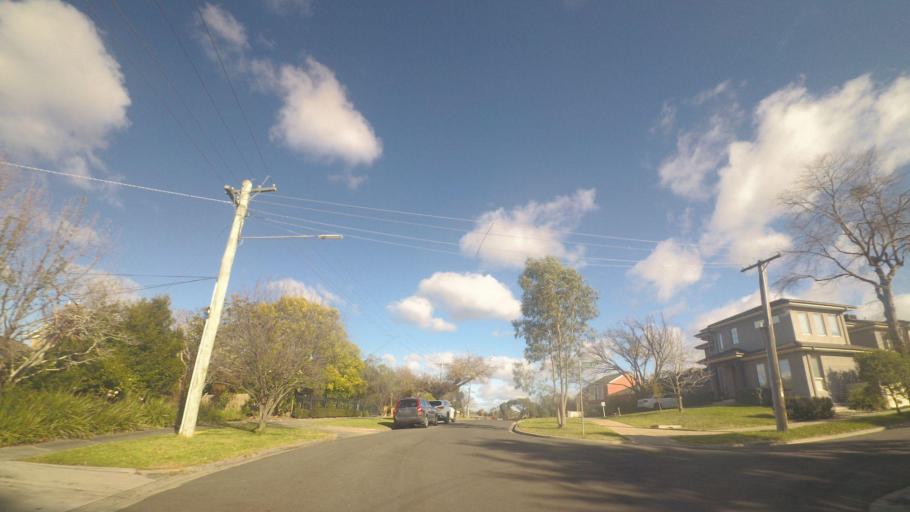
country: AU
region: Victoria
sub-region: Boroondara
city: Balwyn North
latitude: -37.7841
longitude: 145.0901
